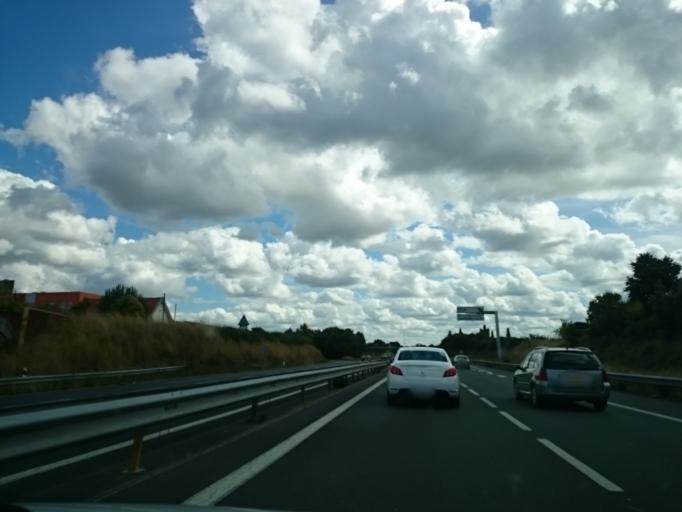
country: FR
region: Pays de la Loire
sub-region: Departement de la Loire-Atlantique
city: Sainte-Luce-sur-Loire
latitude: 47.2557
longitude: -1.4788
